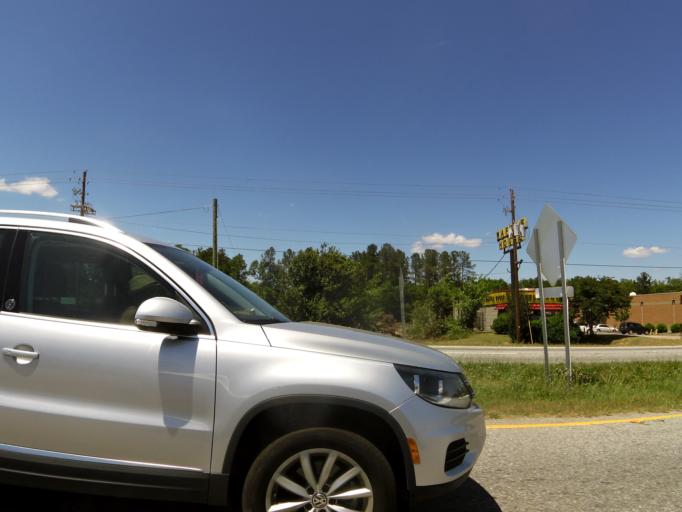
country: US
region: South Carolina
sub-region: Aiken County
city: Clearwater
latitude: 33.5040
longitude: -81.9000
